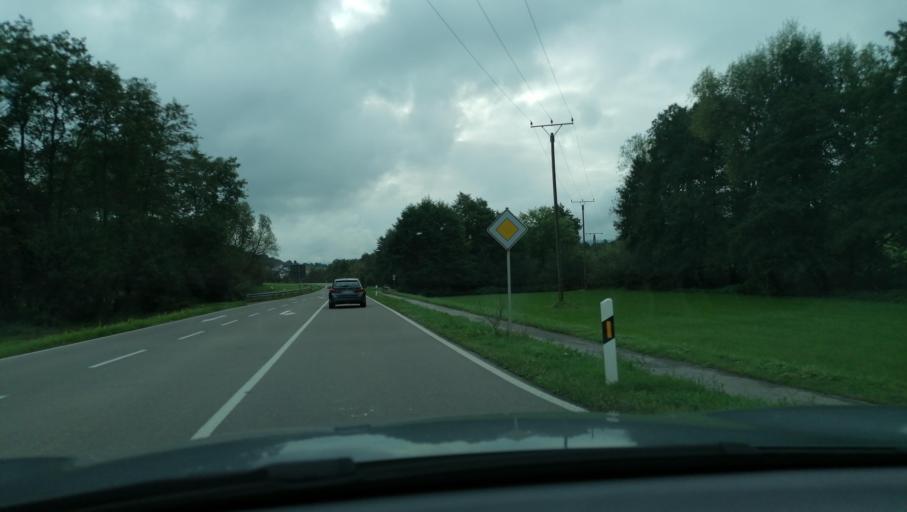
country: DE
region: Baden-Wuerttemberg
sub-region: Regierungsbezirk Stuttgart
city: Schorndorf
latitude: 48.8358
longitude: 9.5013
